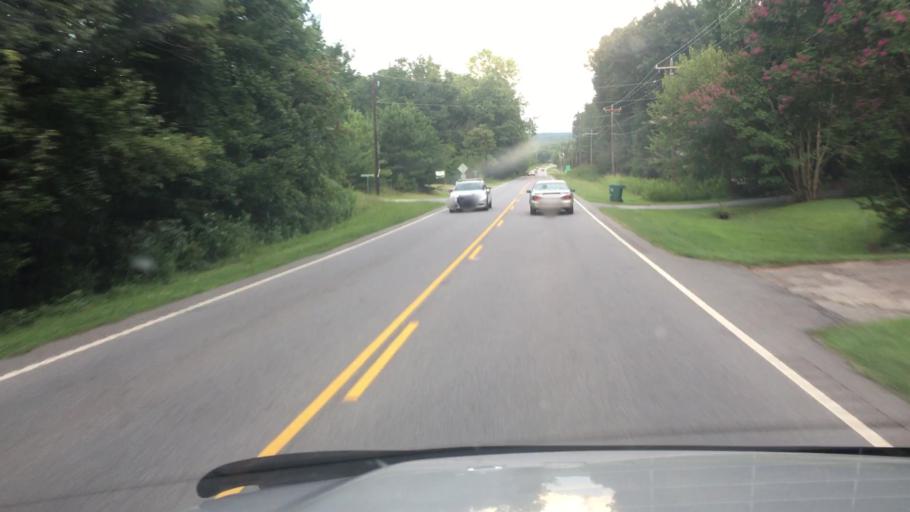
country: US
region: South Carolina
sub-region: Cherokee County
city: Gaffney
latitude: 35.1281
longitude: -81.7361
